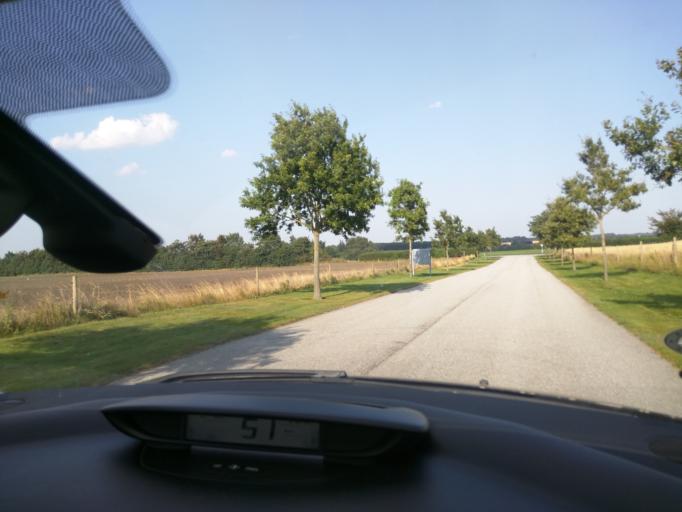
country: DK
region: Central Jutland
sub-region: Viborg Kommune
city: Bjerringbro
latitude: 56.4866
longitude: 9.5944
